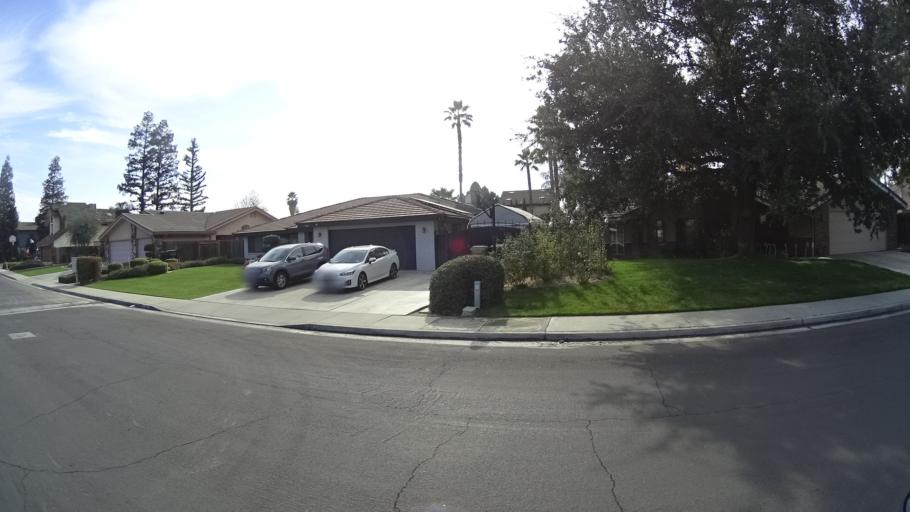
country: US
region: California
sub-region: Kern County
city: Greenacres
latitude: 35.4056
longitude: -119.0802
